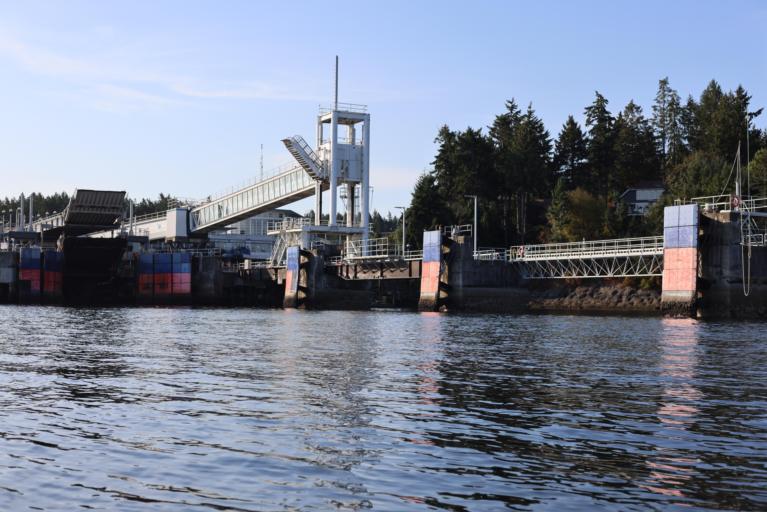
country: CA
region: British Columbia
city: North Saanich
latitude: 48.6907
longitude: -123.4128
